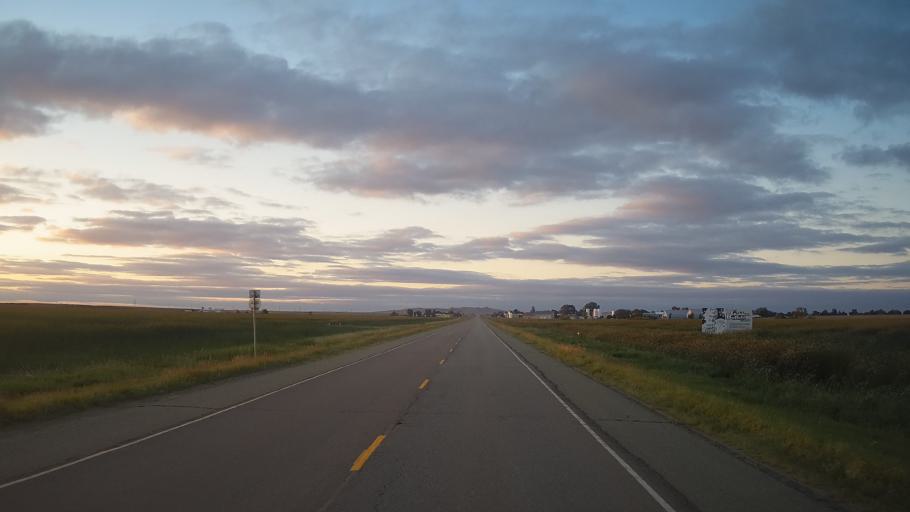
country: US
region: South Dakota
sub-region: Lyman County
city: Kennebec
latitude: 43.8681
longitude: -99.6061
